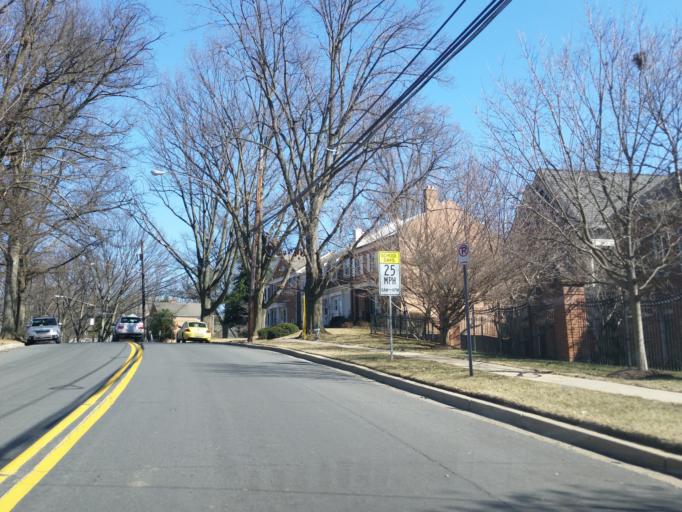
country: US
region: Maryland
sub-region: Montgomery County
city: South Kensington
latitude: 38.9974
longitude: -77.0732
